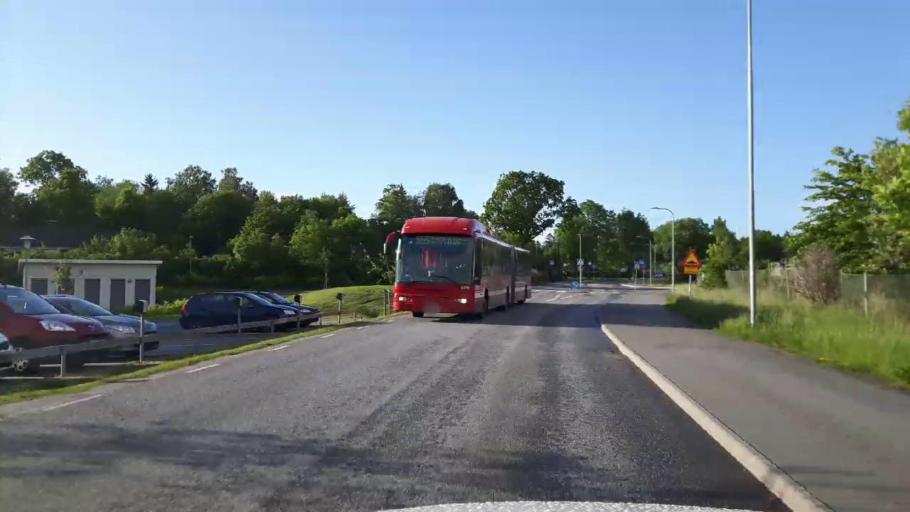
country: SE
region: Stockholm
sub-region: Upplands-Bro Kommun
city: Bro
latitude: 59.5169
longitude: 17.6566
